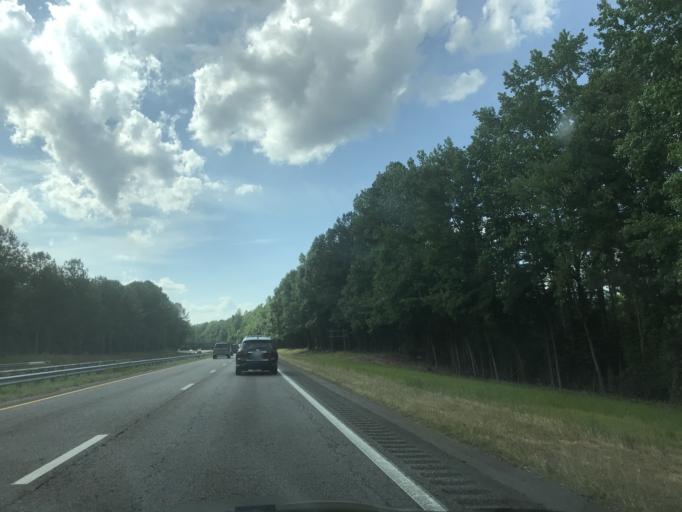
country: US
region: North Carolina
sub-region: Nash County
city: Nashville
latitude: 35.9767
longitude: -77.9515
